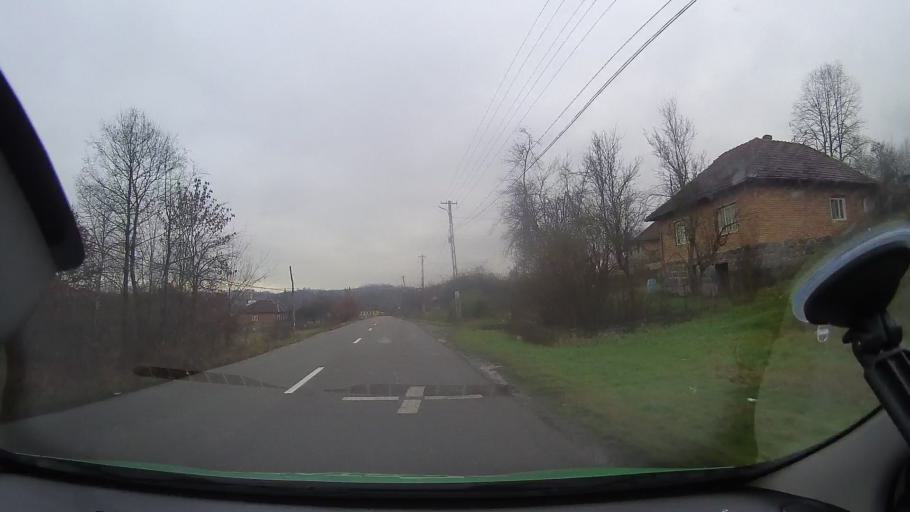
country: RO
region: Arad
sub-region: Comuna Varfurile
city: Varfurile
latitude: 46.3124
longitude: 22.5153
